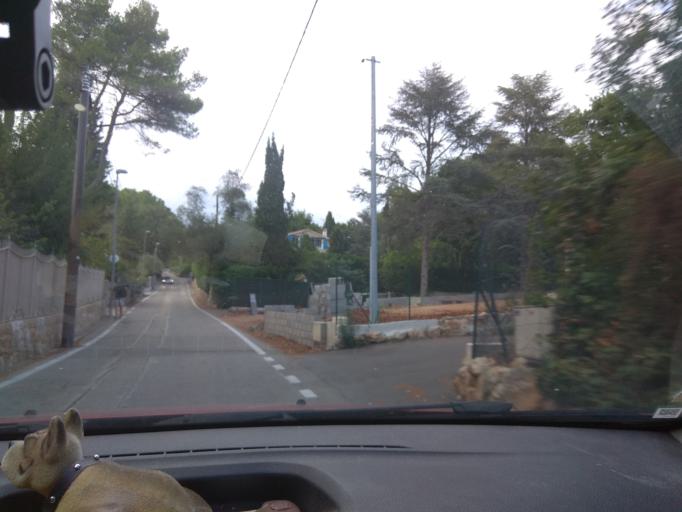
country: FR
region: Provence-Alpes-Cote d'Azur
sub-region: Departement des Alpes-Maritimes
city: Le Rouret
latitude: 43.6716
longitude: 7.0467
